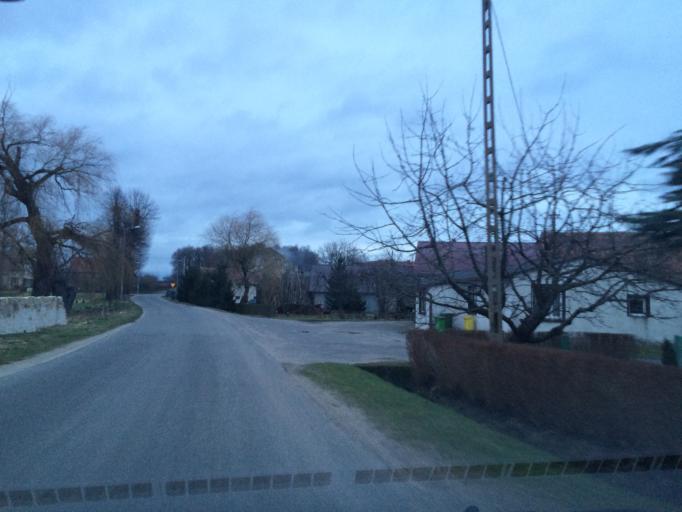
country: PL
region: Lower Silesian Voivodeship
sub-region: Powiat boleslawiecki
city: Nowogrodziec
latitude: 51.2014
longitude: 15.4874
